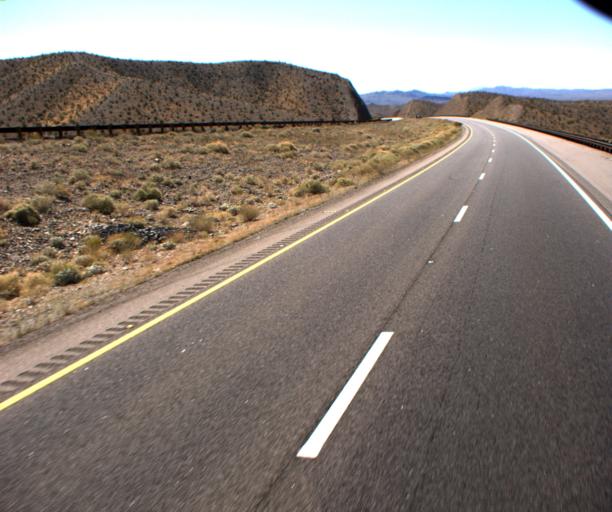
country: US
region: Nevada
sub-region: Clark County
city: Boulder City
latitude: 35.8962
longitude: -114.6260
